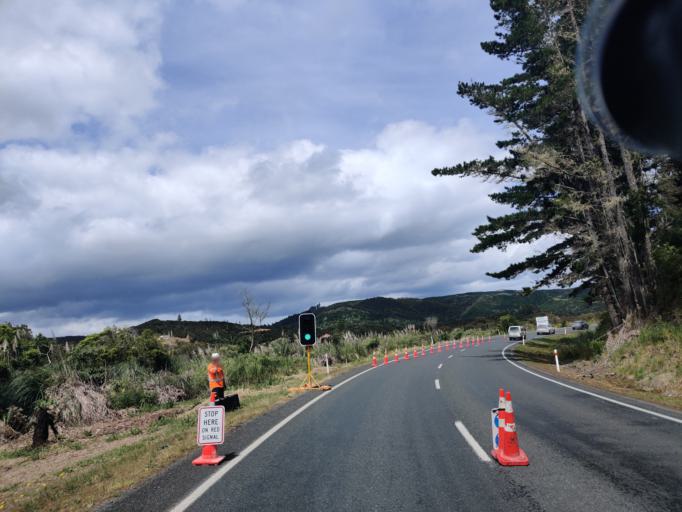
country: NZ
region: Northland
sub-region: Far North District
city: Taipa
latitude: -35.0120
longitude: 173.5546
